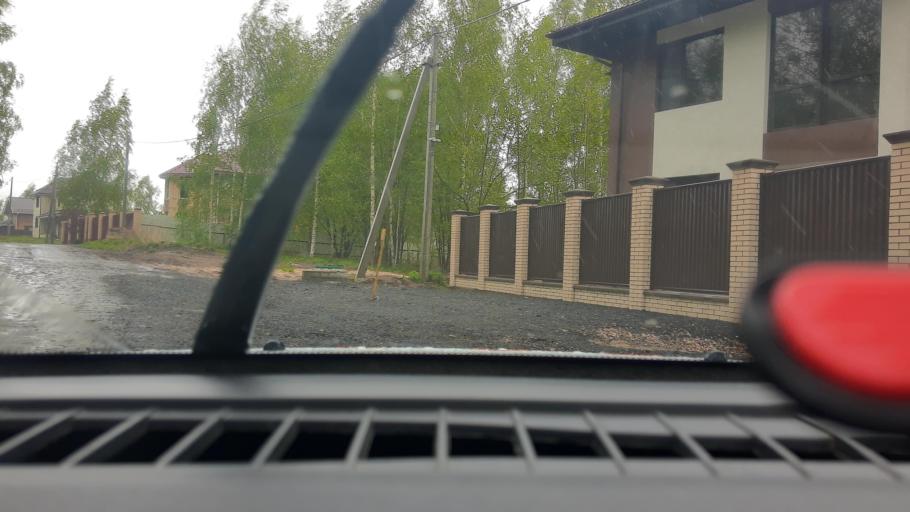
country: RU
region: Nizjnij Novgorod
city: Afonino
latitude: 56.2470
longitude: 44.0713
